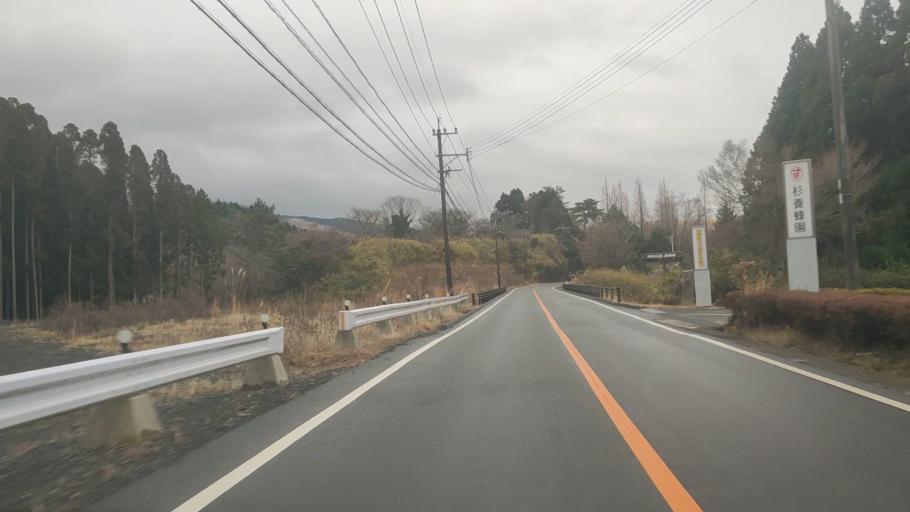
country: JP
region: Kumamoto
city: Aso
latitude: 32.8995
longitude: 131.0170
